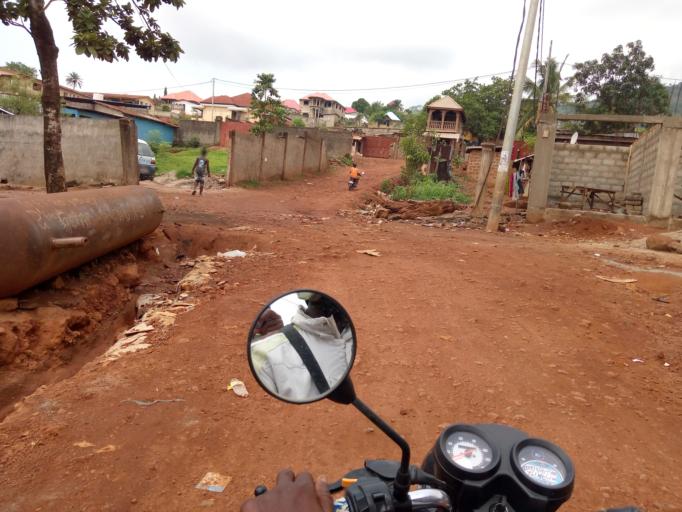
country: SL
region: Western Area
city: Waterloo
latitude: 8.3572
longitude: -13.0822
